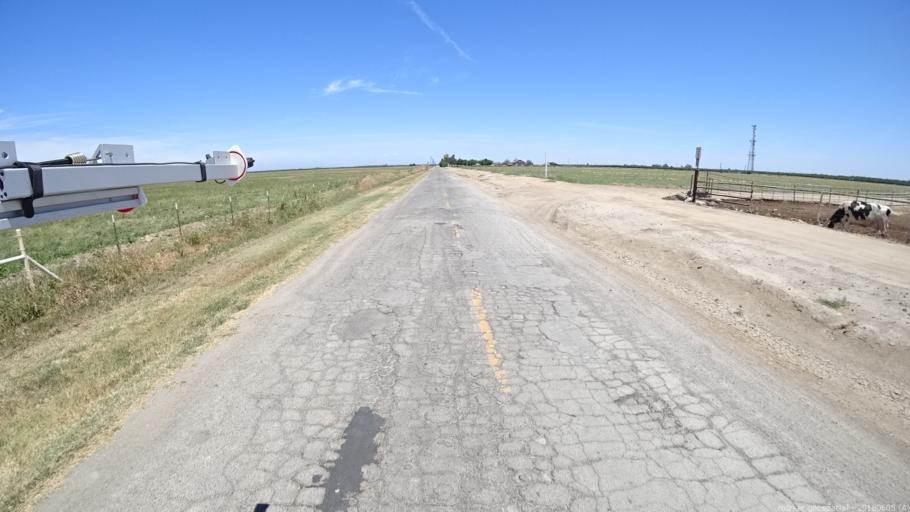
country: US
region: California
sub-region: Madera County
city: Chowchilla
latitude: 37.0907
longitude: -120.3262
